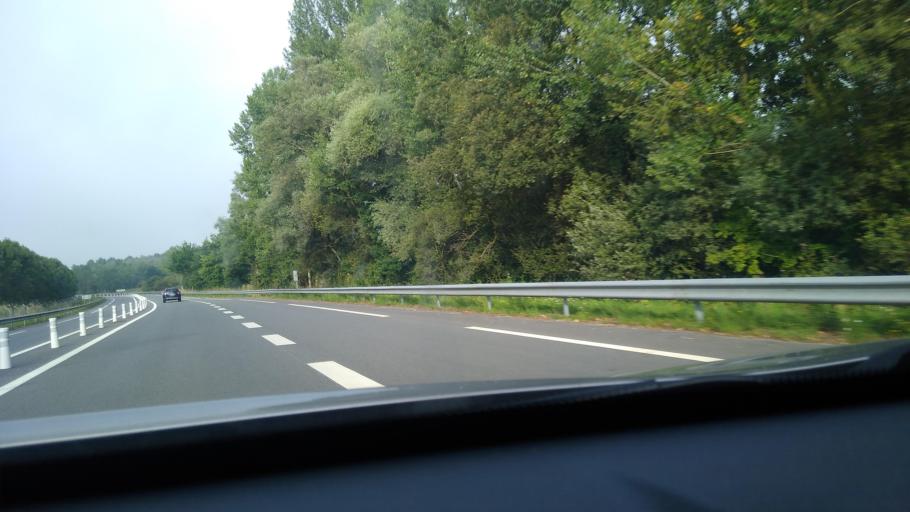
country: FR
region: Midi-Pyrenees
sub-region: Departement de la Haute-Garonne
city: Salies-du-Salat
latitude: 43.1260
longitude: 0.9400
